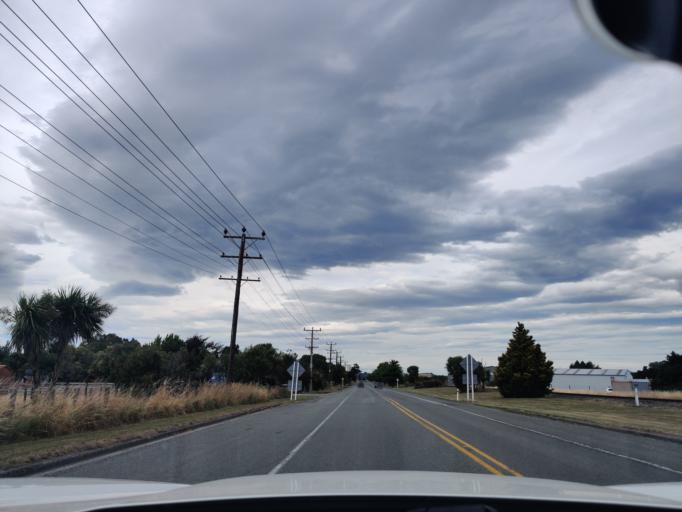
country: NZ
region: Wellington
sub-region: Masterton District
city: Masterton
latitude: -40.9571
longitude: 175.6155
